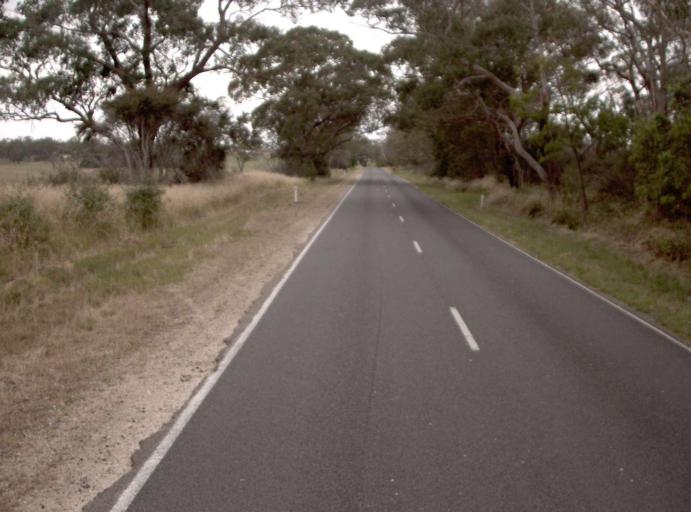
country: AU
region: Victoria
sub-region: Wellington
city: Sale
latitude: -38.1743
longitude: 147.1177
